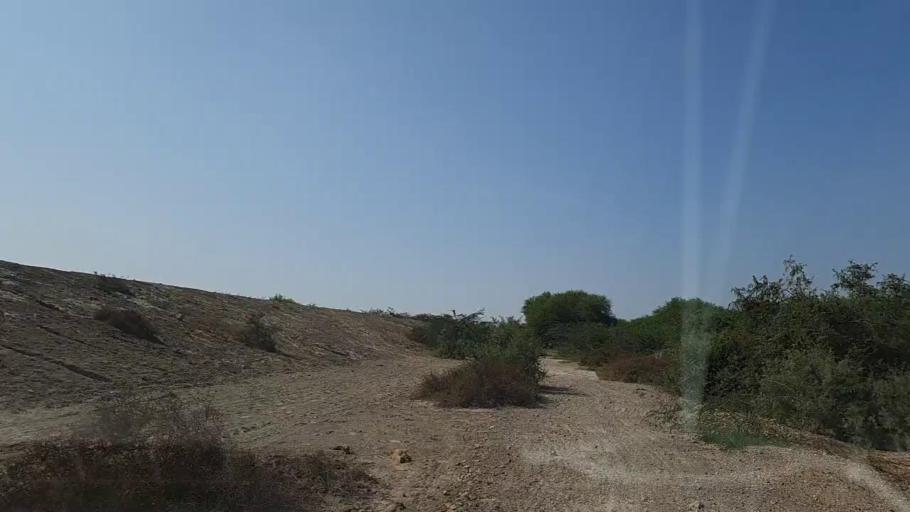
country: PK
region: Sindh
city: Chuhar Jamali
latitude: 24.4895
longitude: 68.0110
